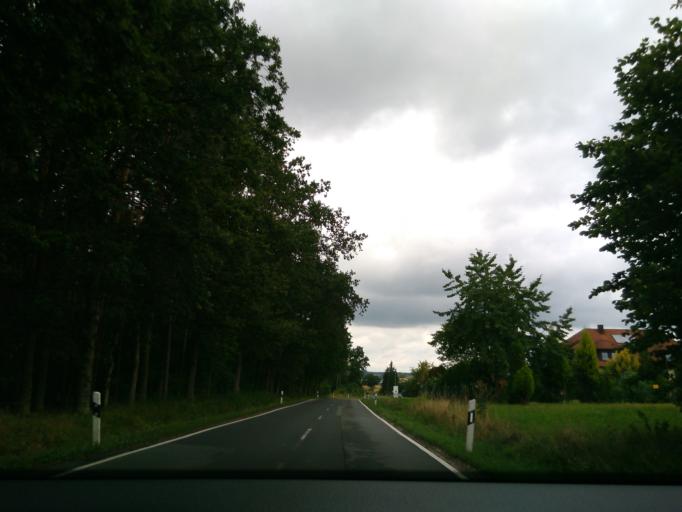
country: DE
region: Bavaria
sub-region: Regierungsbezirk Mittelfranken
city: Hochstadt an der Aisch
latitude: 49.6869
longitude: 10.8051
